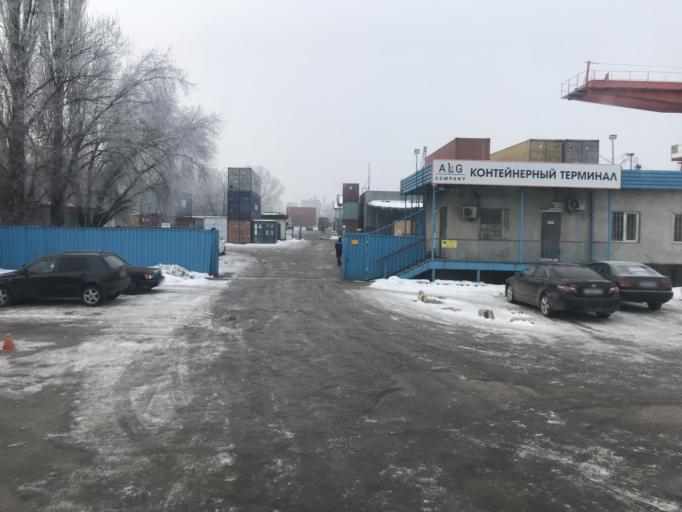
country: KZ
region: Almaty Oblysy
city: Pervomayskiy
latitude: 43.3581
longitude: 76.9730
